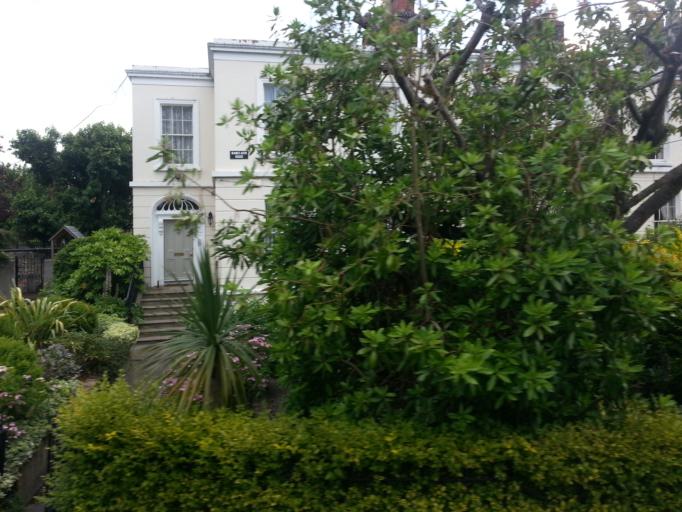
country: IE
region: Leinster
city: Rathmines
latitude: 53.3279
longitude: -6.2585
